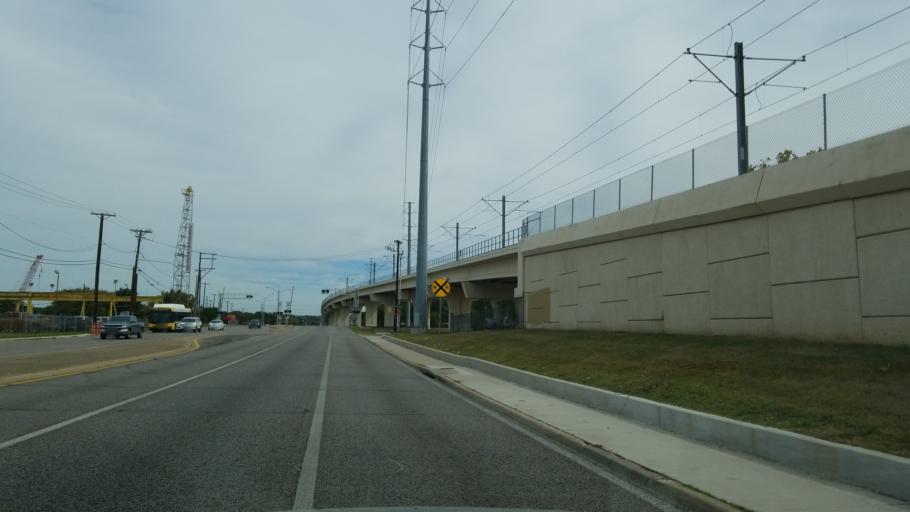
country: US
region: Texas
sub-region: Dallas County
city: Dallas
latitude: 32.7663
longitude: -96.7393
